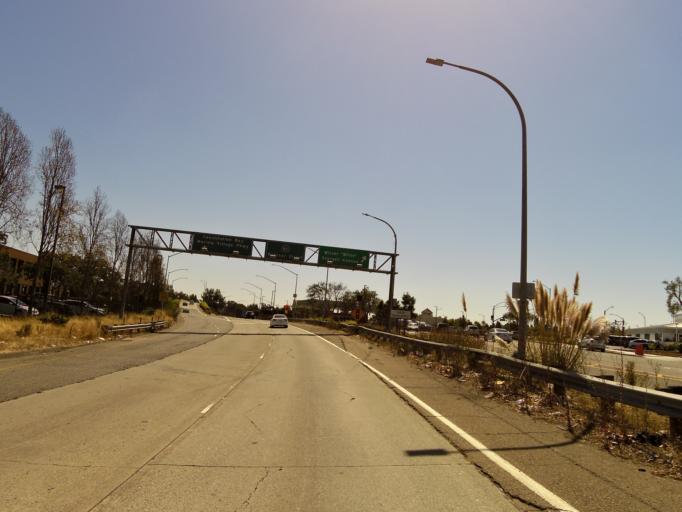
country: US
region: California
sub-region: Alameda County
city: Oakland
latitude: 37.7863
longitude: -122.2784
